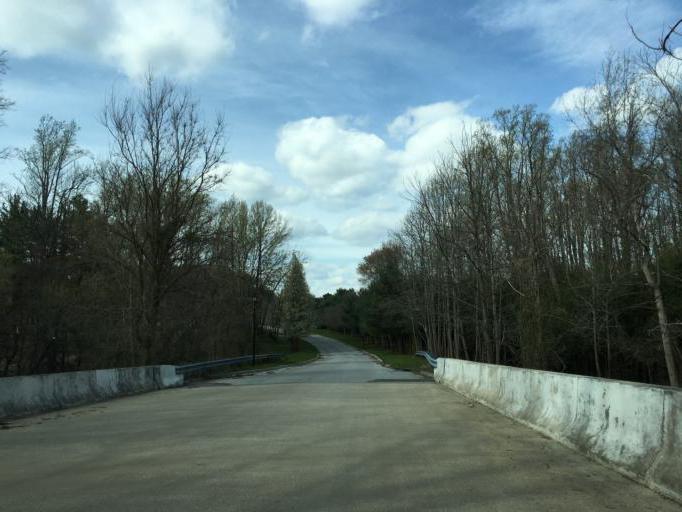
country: US
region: Maryland
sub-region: Baltimore County
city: Cockeysville
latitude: 39.4776
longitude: -76.6748
